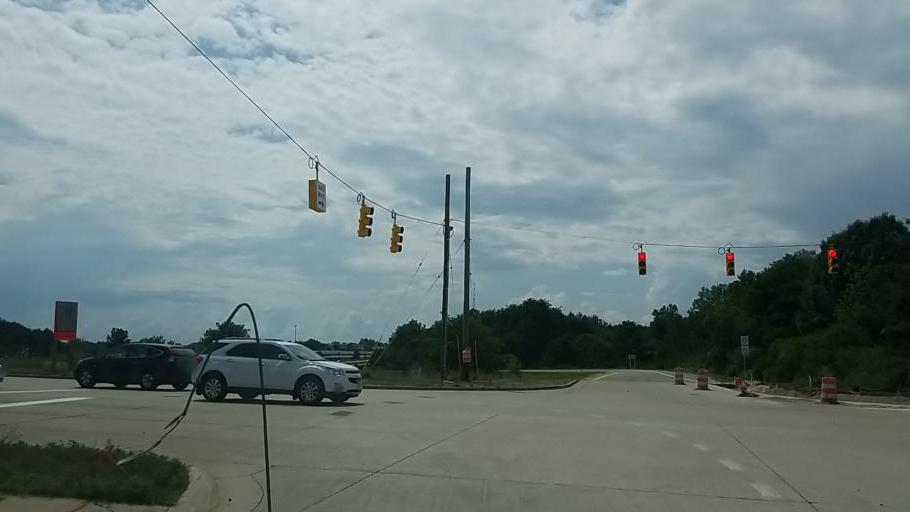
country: US
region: Michigan
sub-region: Kent County
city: Walker
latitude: 43.0227
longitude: -85.7260
